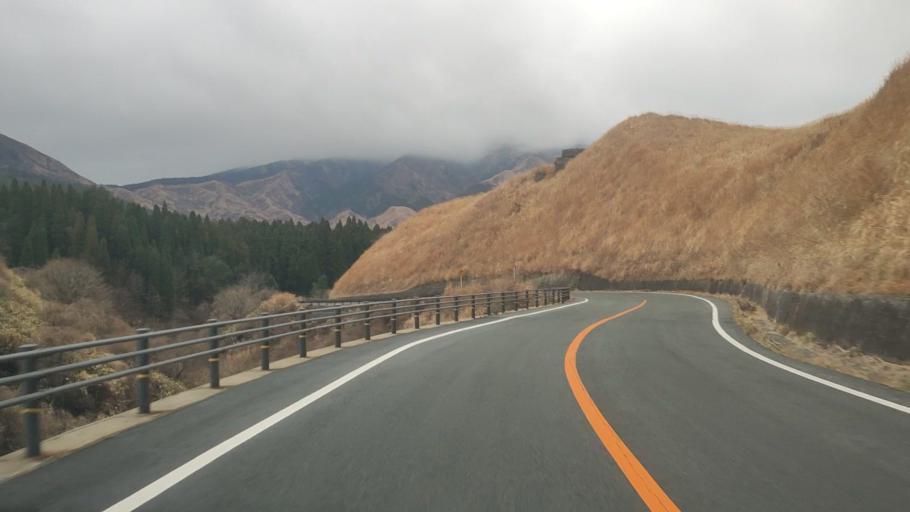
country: JP
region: Kumamoto
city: Aso
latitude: 32.9052
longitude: 131.1465
